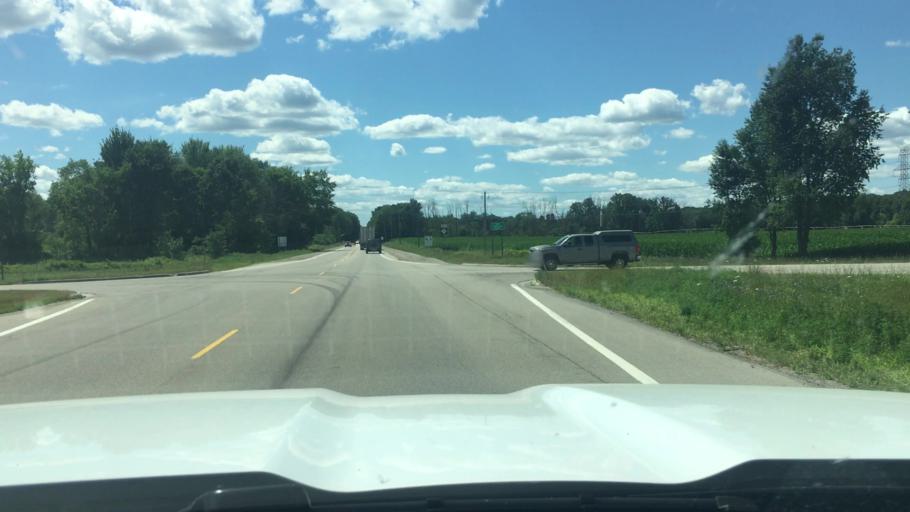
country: US
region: Michigan
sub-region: Kent County
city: Cedar Springs
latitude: 43.1764
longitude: -85.4309
